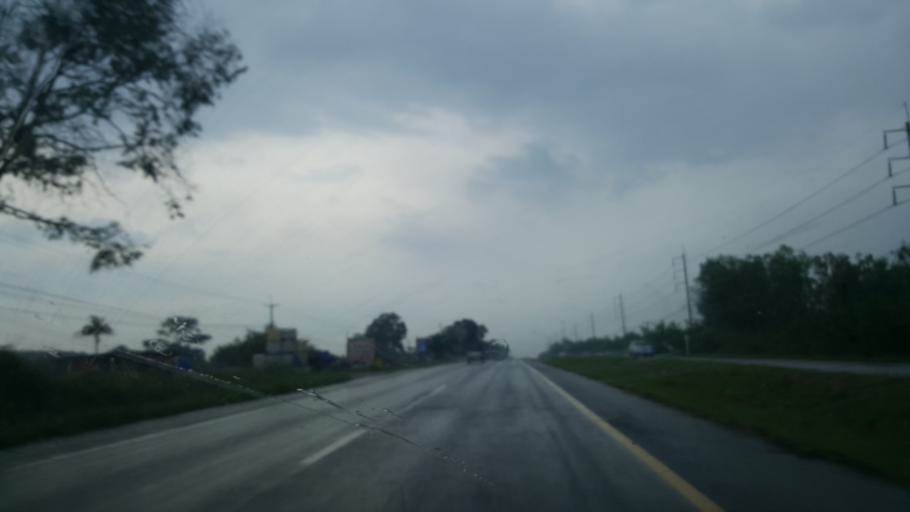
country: TH
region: Chon Buri
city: Ban Talat Bueng
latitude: 12.9678
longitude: 101.0543
